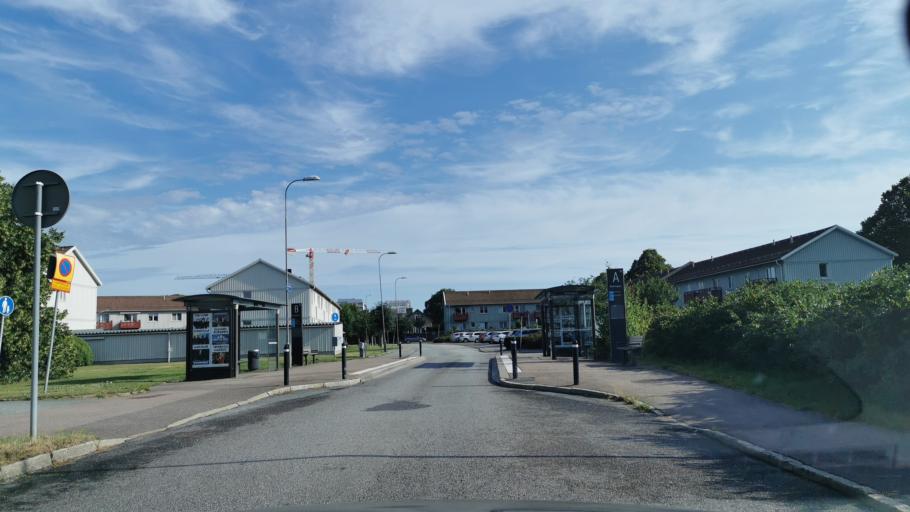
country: SE
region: Vaestra Goetaland
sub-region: Goteborg
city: Majorna
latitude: 57.6529
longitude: 11.9318
